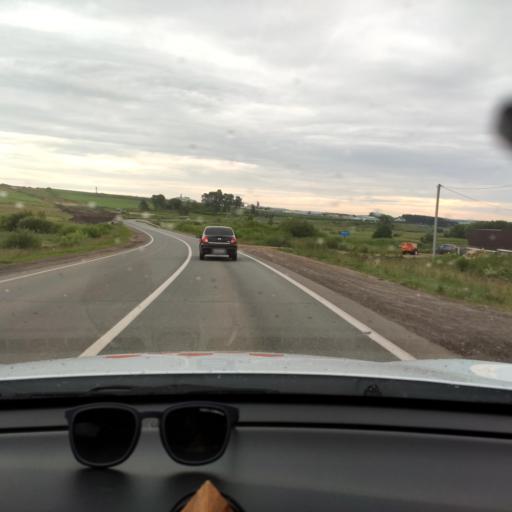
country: RU
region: Tatarstan
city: Pestretsy
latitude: 55.8306
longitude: 49.6752
